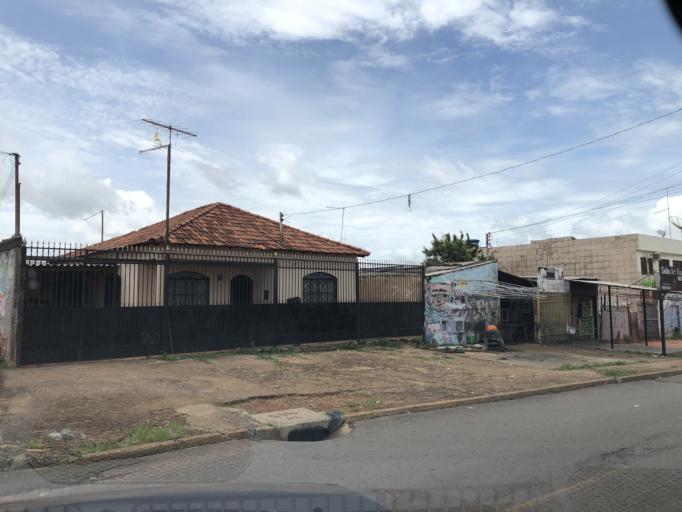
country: BR
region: Federal District
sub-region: Brasilia
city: Brasilia
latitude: -15.8178
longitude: -48.1192
